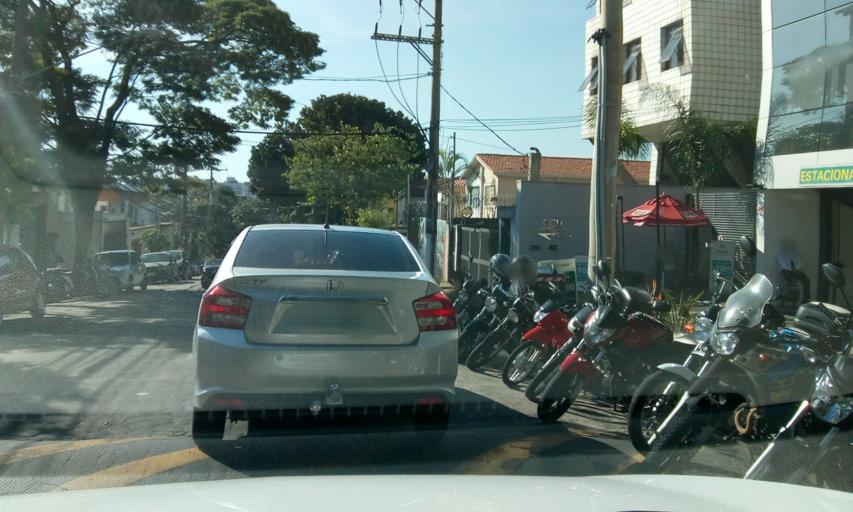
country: BR
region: Sao Paulo
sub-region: Diadema
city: Diadema
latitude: -23.6211
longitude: -46.6629
